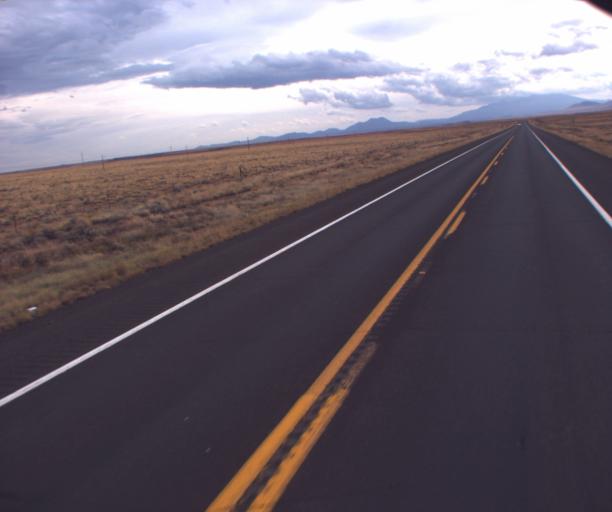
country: US
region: Arizona
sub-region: Coconino County
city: Tuba City
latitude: 35.7392
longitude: -111.4765
